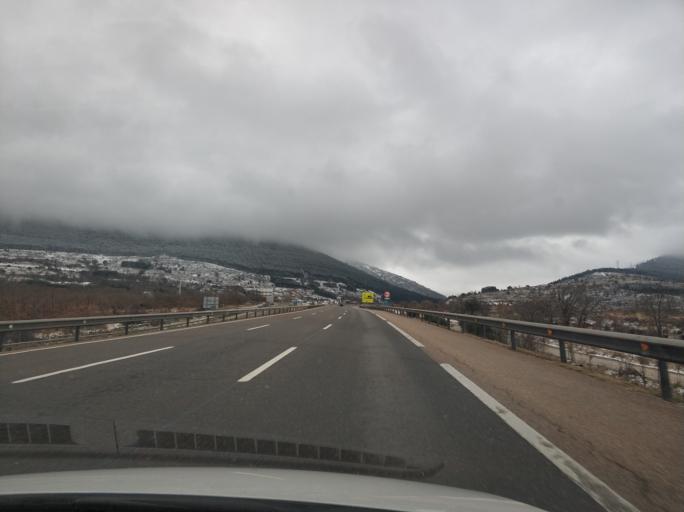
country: ES
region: Castille and Leon
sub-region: Provincia de Segovia
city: Cerezo de Abajo
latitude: 41.1813
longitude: -3.5842
